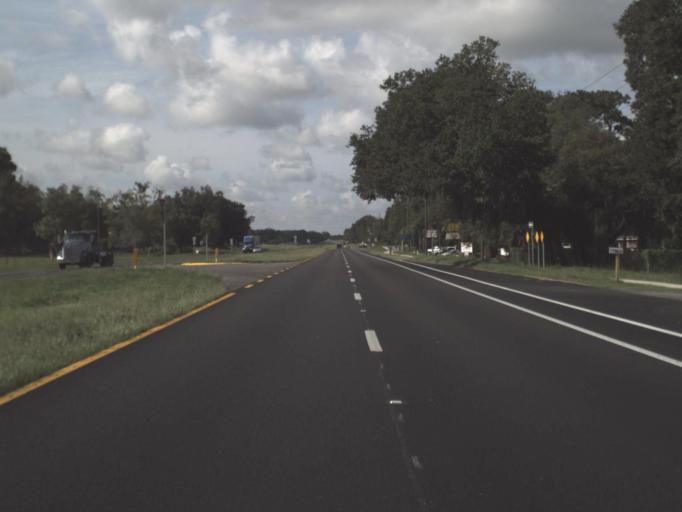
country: US
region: Florida
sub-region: Pasco County
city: Lacoochee
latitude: 28.4533
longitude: -82.1865
